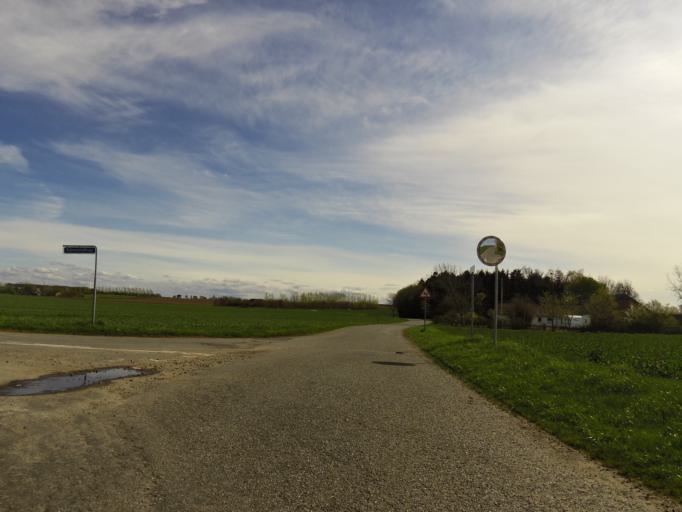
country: DK
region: Central Jutland
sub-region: Skive Kommune
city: Skive
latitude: 56.5504
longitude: 8.9621
